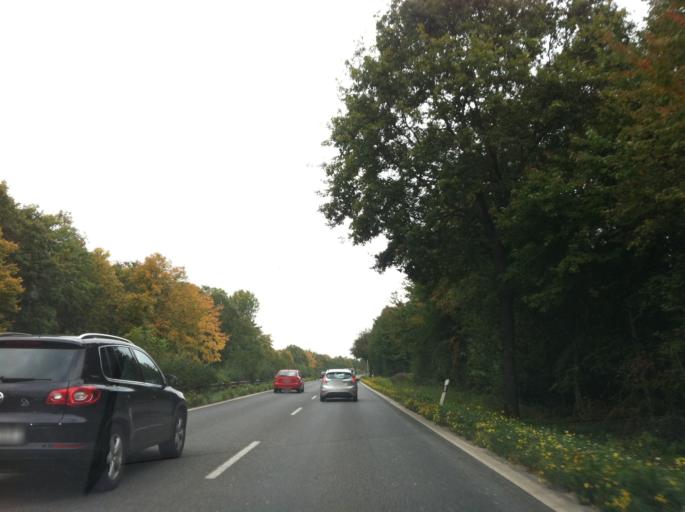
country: DE
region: North Rhine-Westphalia
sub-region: Regierungsbezirk Koln
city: Dueren
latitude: 50.8308
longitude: 6.4670
